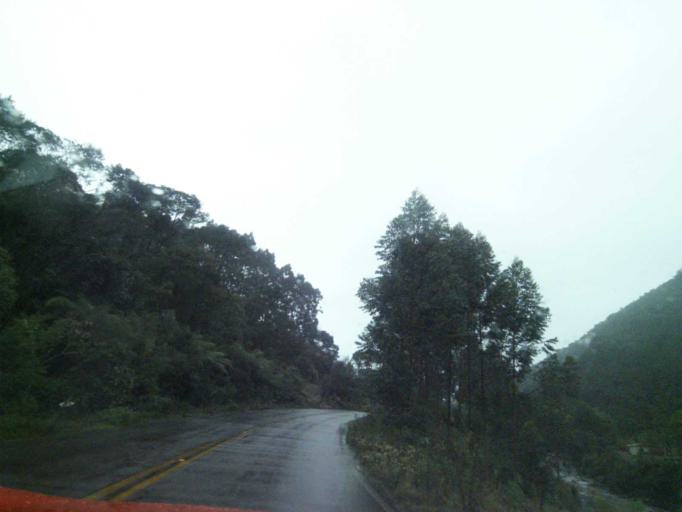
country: BR
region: Santa Catarina
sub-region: Anitapolis
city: Anitapolis
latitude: -27.8059
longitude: -49.0465
